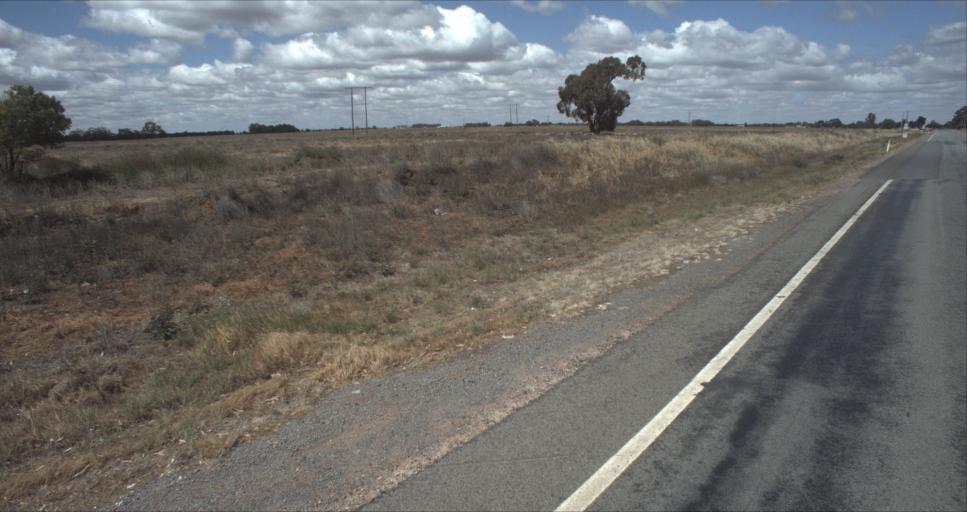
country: AU
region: New South Wales
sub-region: Murrumbidgee Shire
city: Darlington Point
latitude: -34.5080
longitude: 146.1869
